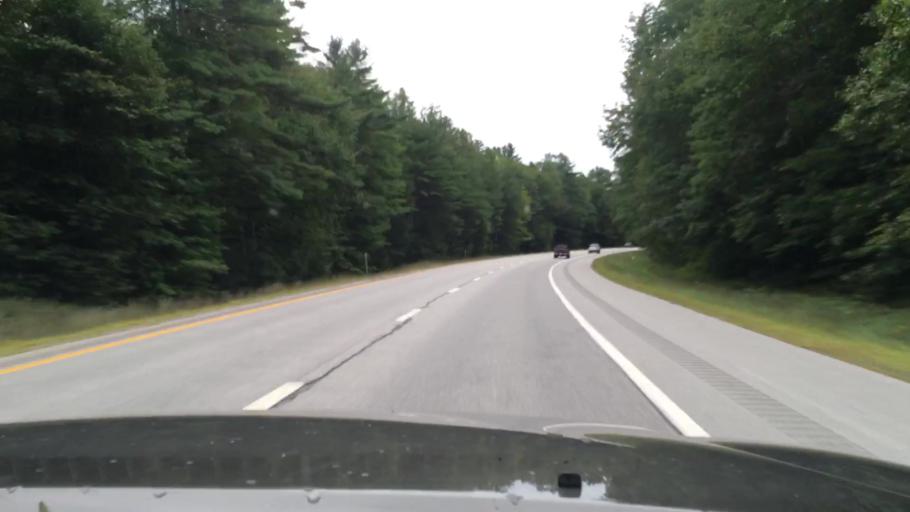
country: US
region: New Hampshire
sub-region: Belknap County
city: Sanbornton
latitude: 43.5167
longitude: -71.6166
